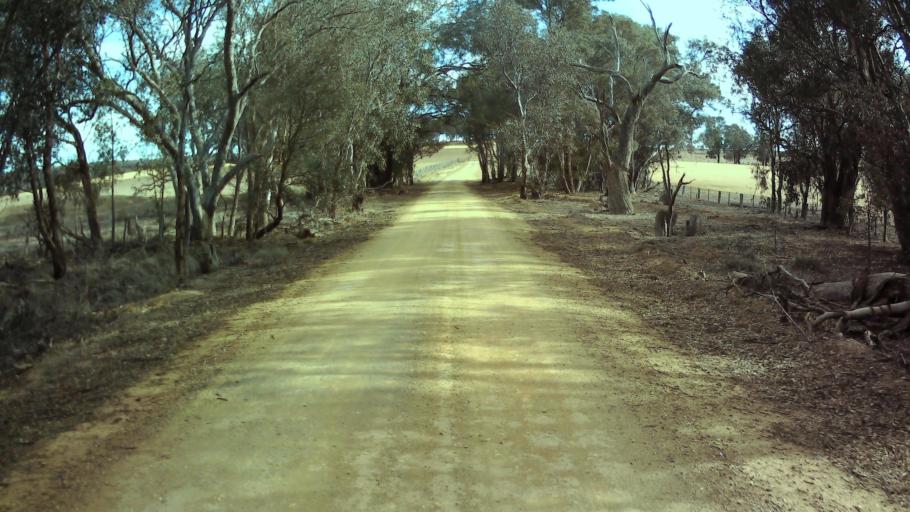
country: AU
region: New South Wales
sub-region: Weddin
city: Grenfell
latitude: -33.8987
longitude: 148.2034
